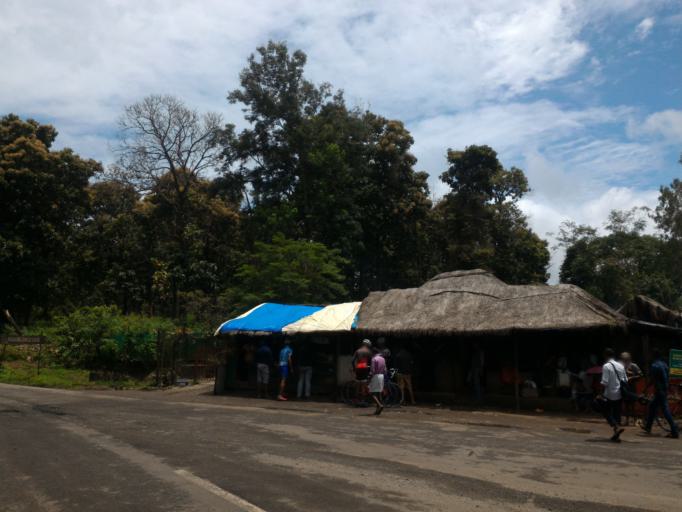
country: IN
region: Kerala
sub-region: Wayanad
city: Panamaram
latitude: 11.9025
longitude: 76.0671
